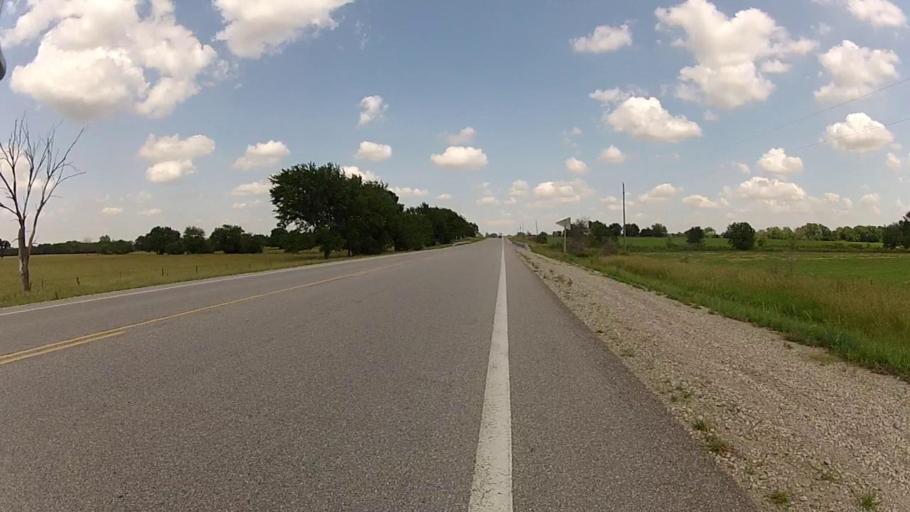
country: US
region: Kansas
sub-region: Labette County
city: Oswego
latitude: 37.1935
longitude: -95.1708
